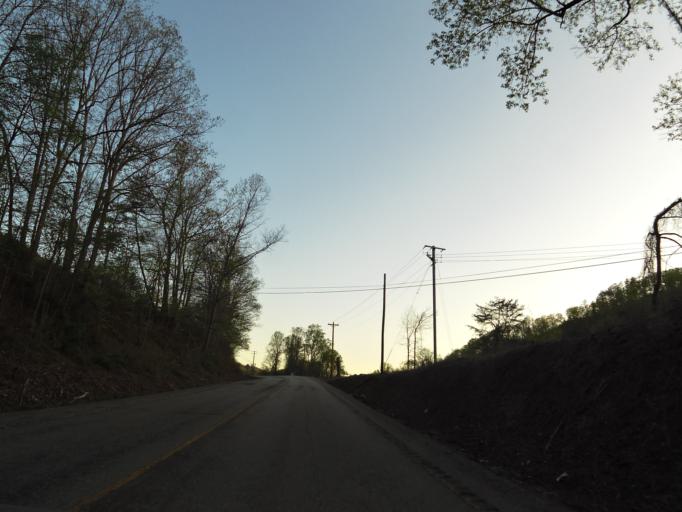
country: US
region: Tennessee
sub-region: Campbell County
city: Fincastle
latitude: 36.4370
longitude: -84.0780
